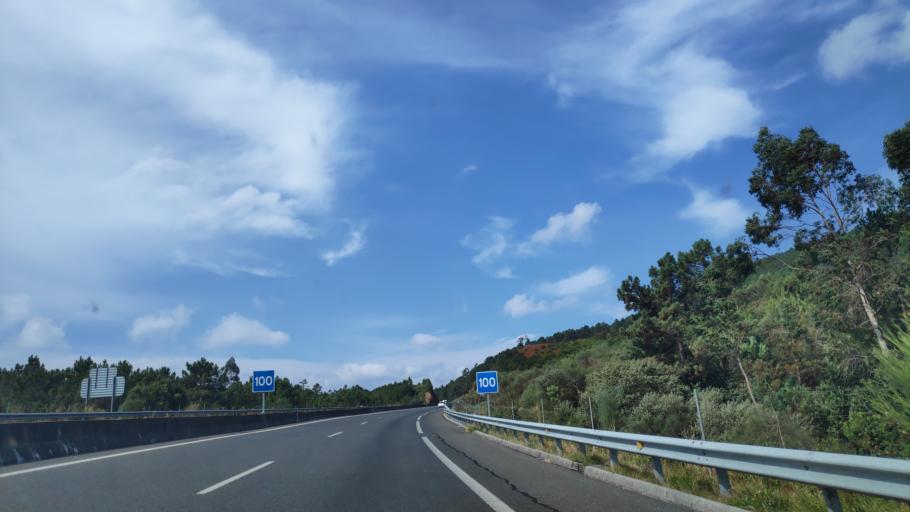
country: ES
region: Galicia
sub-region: Provincia de Pontevedra
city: Catoira
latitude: 42.7032
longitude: -8.7328
